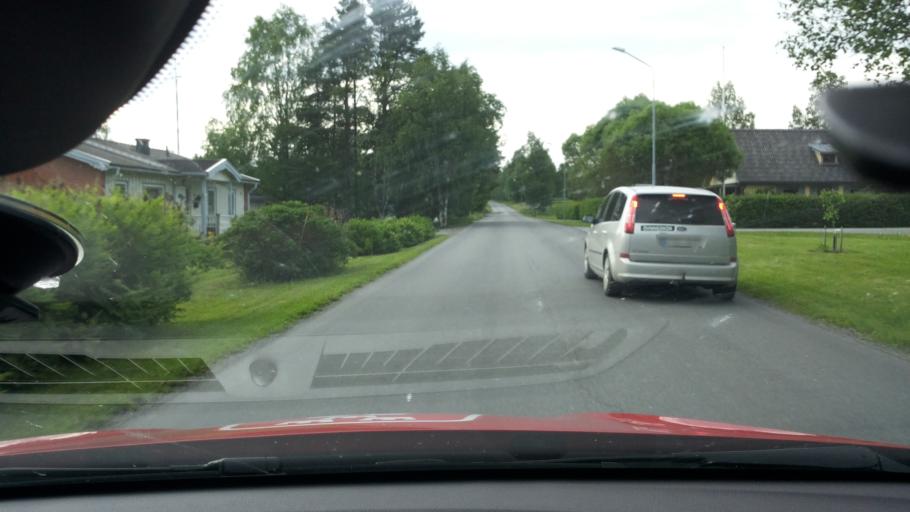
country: SE
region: Jaemtland
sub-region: Bergs Kommun
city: Hoverberg
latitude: 62.9325
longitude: 14.5156
